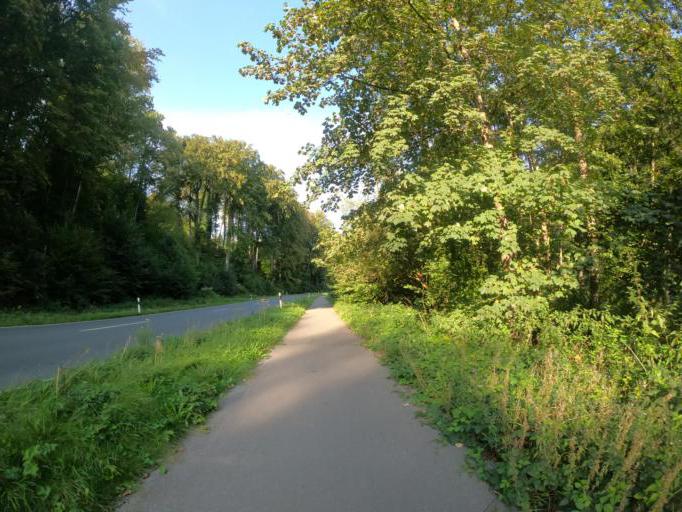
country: DE
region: North Rhine-Westphalia
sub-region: Regierungsbezirk Dusseldorf
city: Mettmann
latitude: 51.2299
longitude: 6.9650
